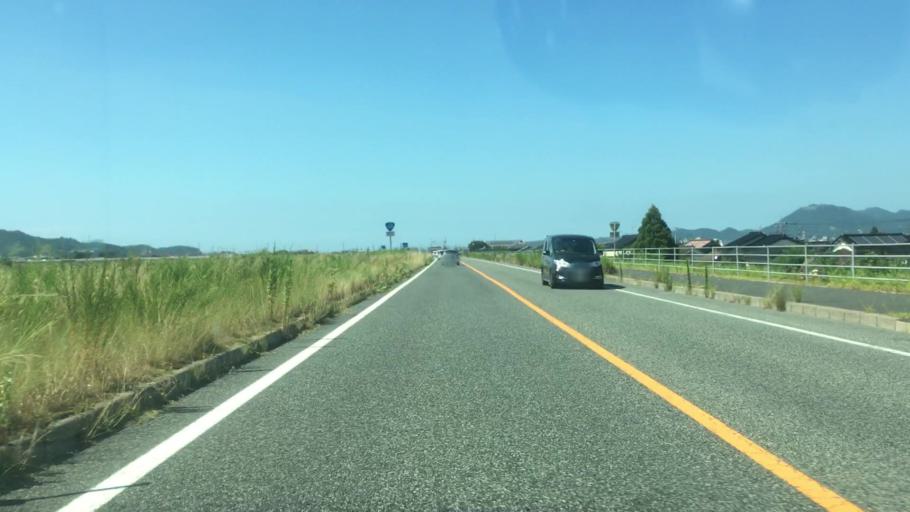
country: JP
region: Tottori
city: Tottori
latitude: 35.4572
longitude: 134.2152
